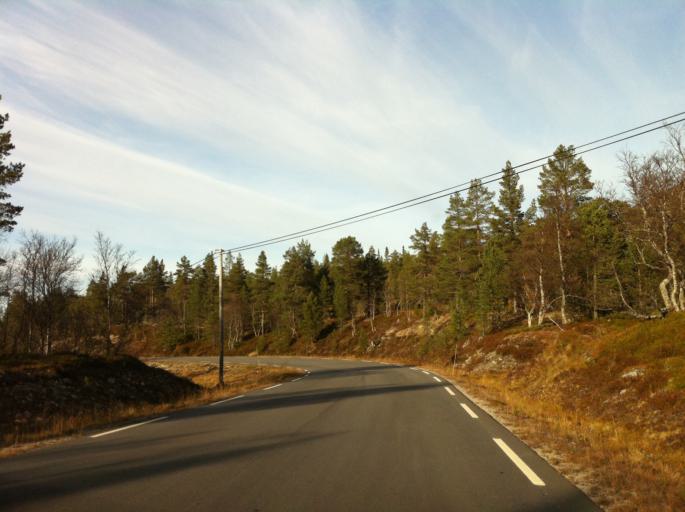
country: NO
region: Hedmark
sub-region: Engerdal
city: Engerdal
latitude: 62.0898
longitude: 12.0498
